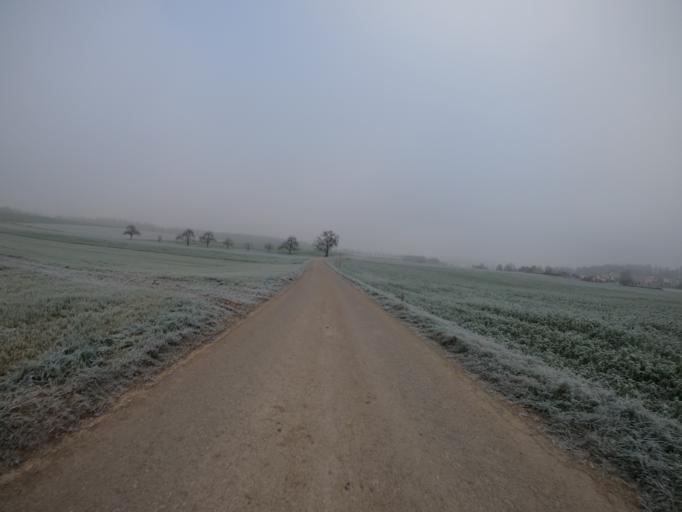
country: DE
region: Baden-Wuerttemberg
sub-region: Tuebingen Region
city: Westerstetten
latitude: 48.5051
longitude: 9.9471
